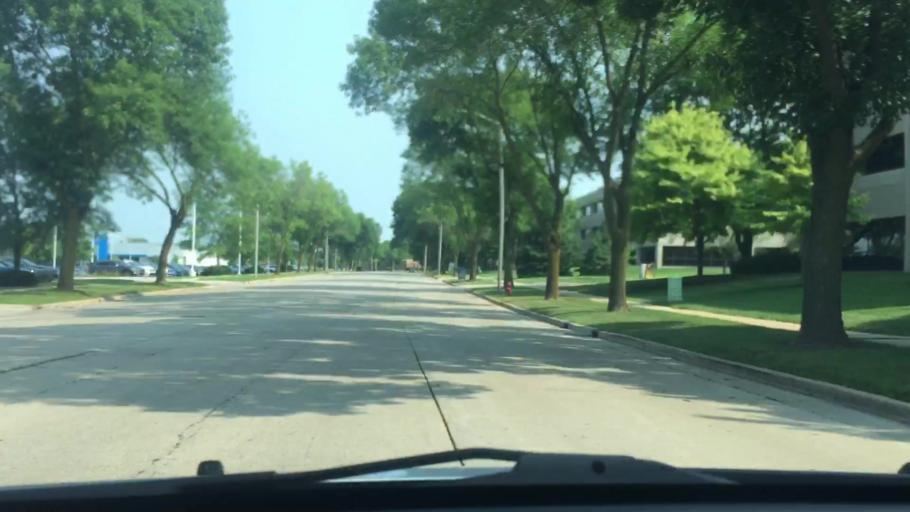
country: US
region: Wisconsin
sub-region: Milwaukee County
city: West Allis
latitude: 42.9974
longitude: -88.0419
